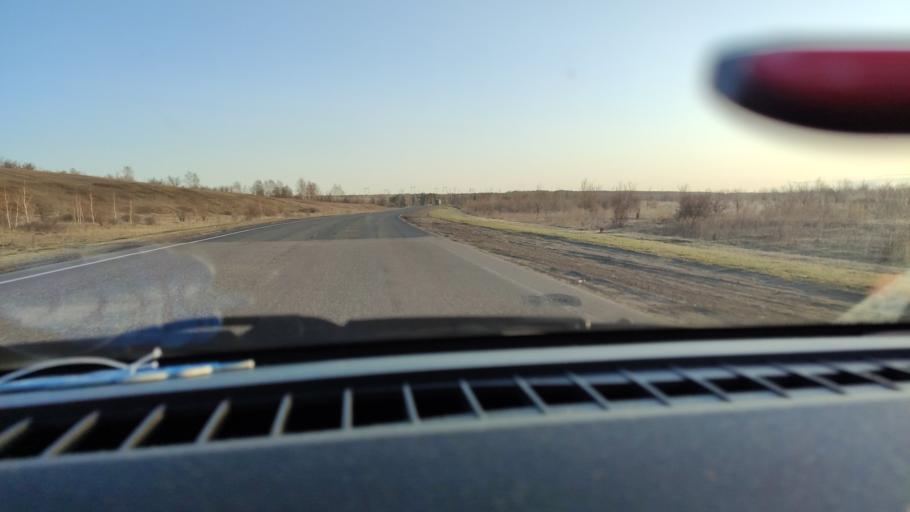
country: RU
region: Saratov
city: Sennoy
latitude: 52.0973
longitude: 46.8129
